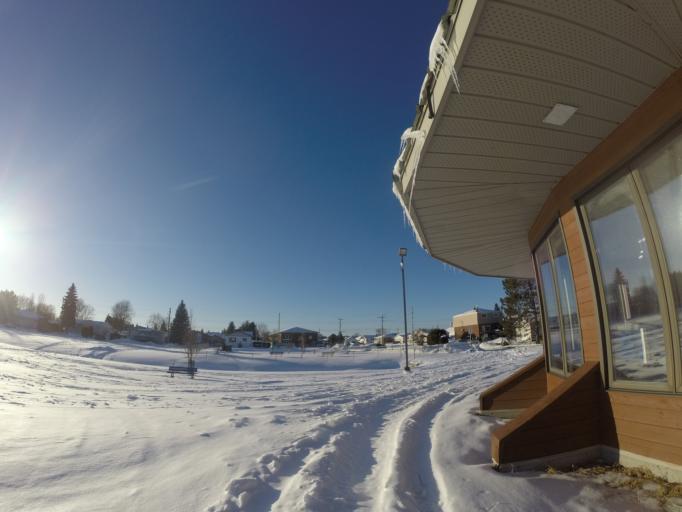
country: CA
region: Ontario
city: Rayside-Balfour
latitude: 46.5757
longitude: -81.1944
